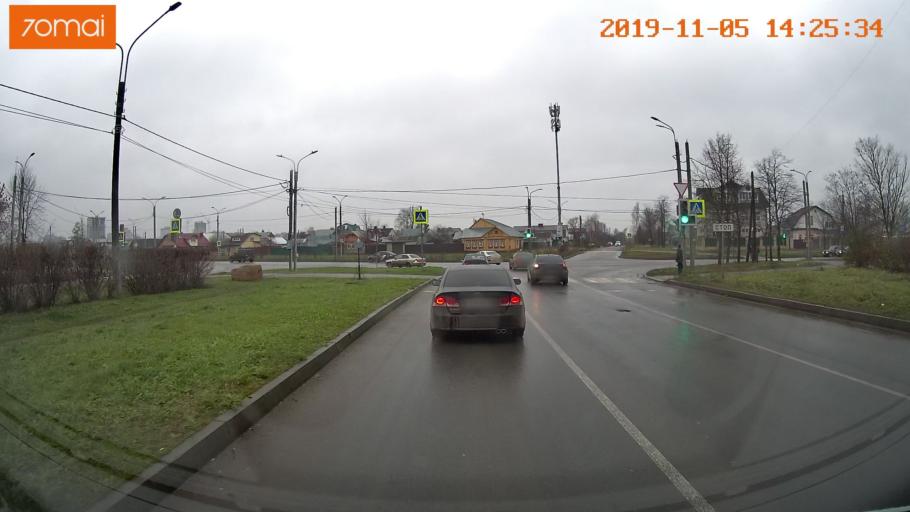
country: RU
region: Ivanovo
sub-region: Gorod Ivanovo
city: Ivanovo
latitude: 56.9710
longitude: 40.9936
